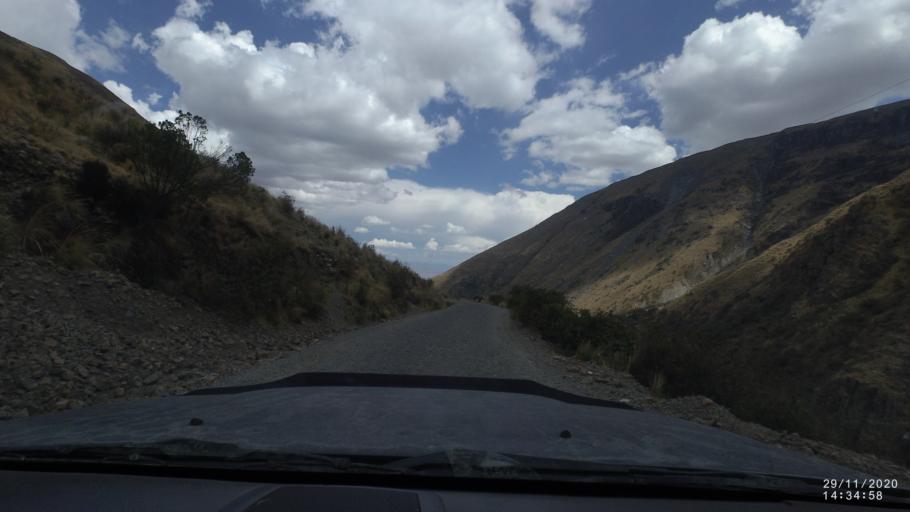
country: BO
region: Cochabamba
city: Sipe Sipe
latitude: -17.2690
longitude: -66.3399
